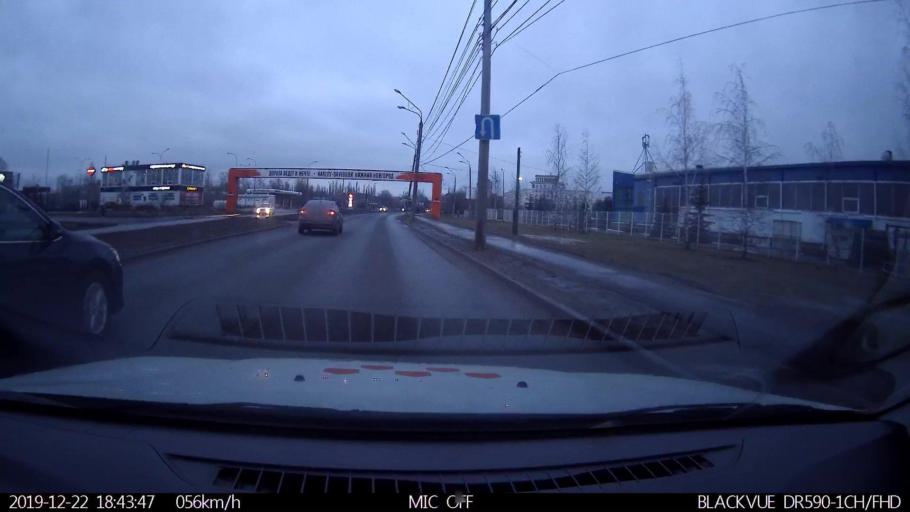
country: RU
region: Nizjnij Novgorod
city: Nizhniy Novgorod
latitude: 56.3397
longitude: 43.8879
